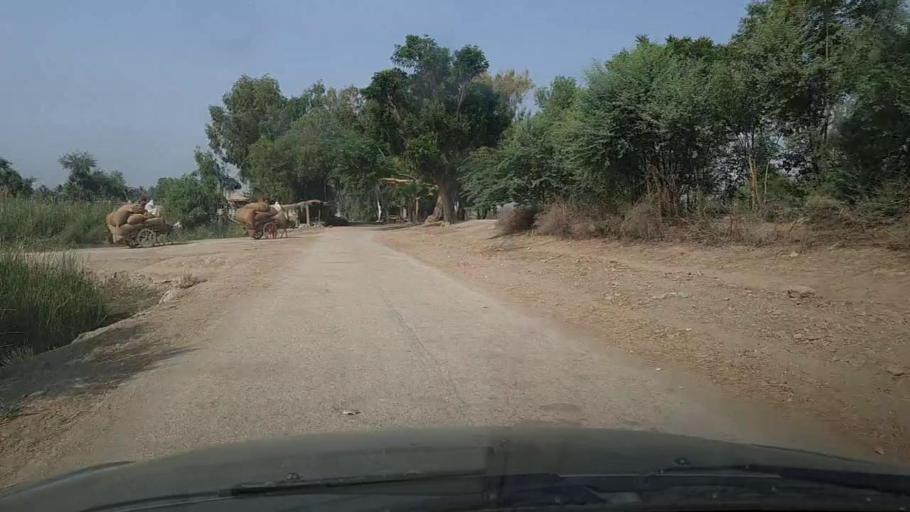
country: PK
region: Sindh
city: Pir jo Goth
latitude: 27.5276
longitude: 68.4966
